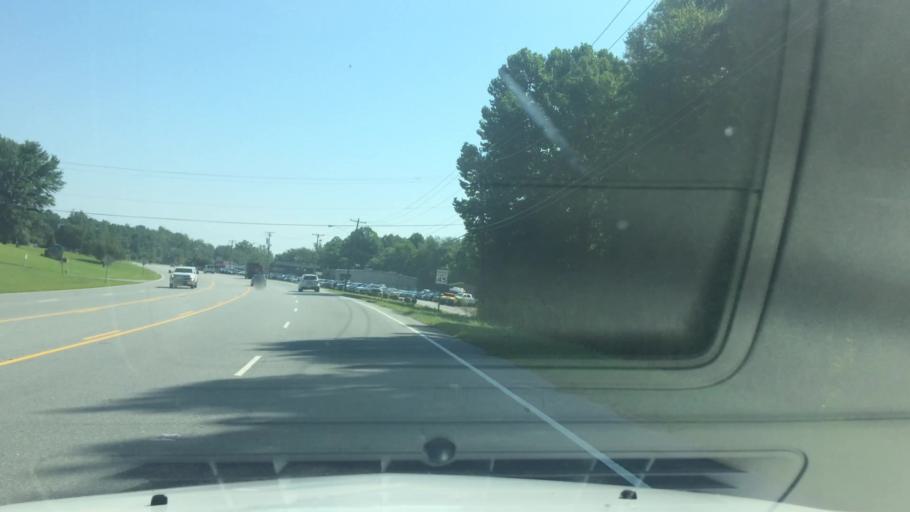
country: US
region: North Carolina
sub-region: Caldwell County
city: Lenoir
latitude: 35.9204
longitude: -81.5080
